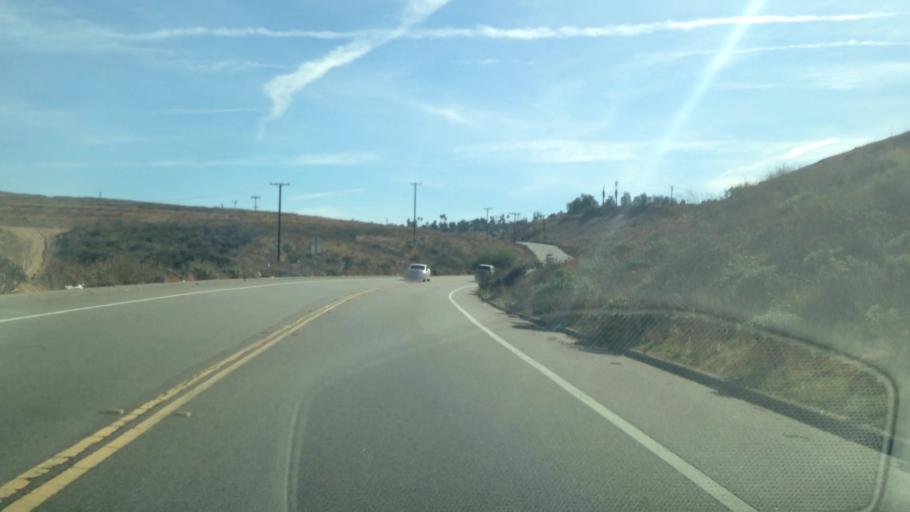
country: US
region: California
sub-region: Riverside County
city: Highgrove
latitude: 33.9651
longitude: -117.3129
